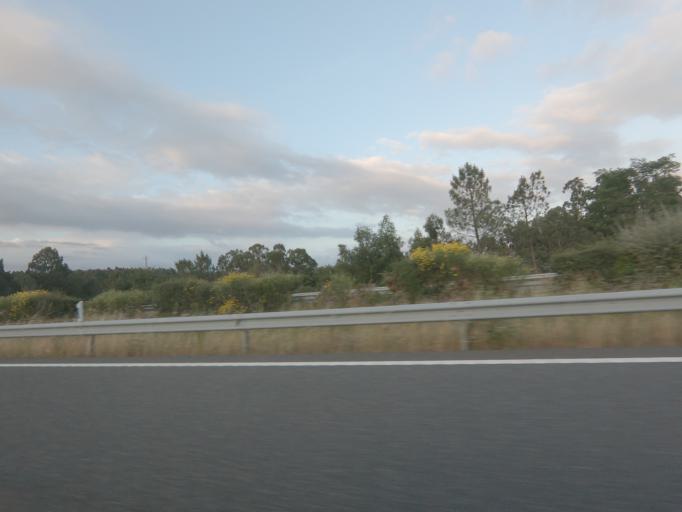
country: ES
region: Galicia
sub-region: Provincia de Ourense
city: Melon
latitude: 42.2093
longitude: -8.2650
